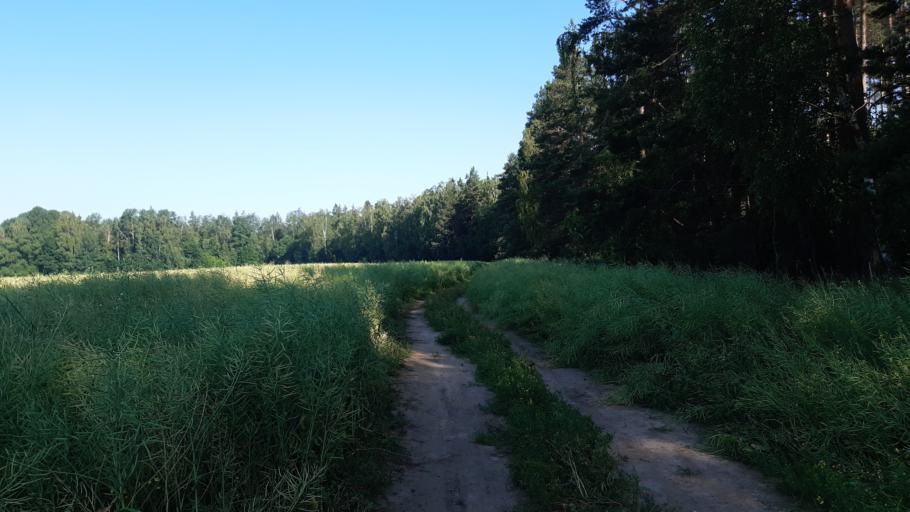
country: BY
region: Minsk
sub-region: Smalyavitski Rayon
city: Oktjabr'skij
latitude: 54.1009
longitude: 28.2354
